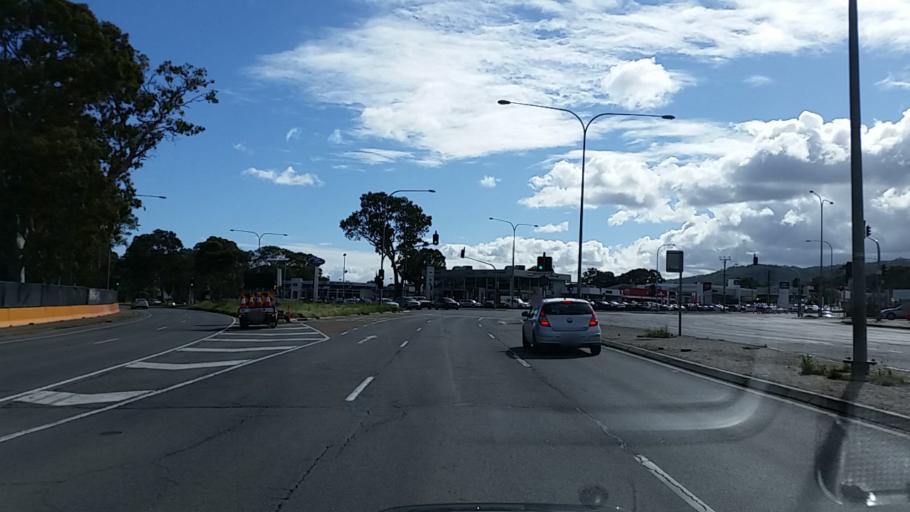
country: AU
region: South Australia
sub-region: Marion
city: Marion
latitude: -35.0117
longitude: 138.5753
